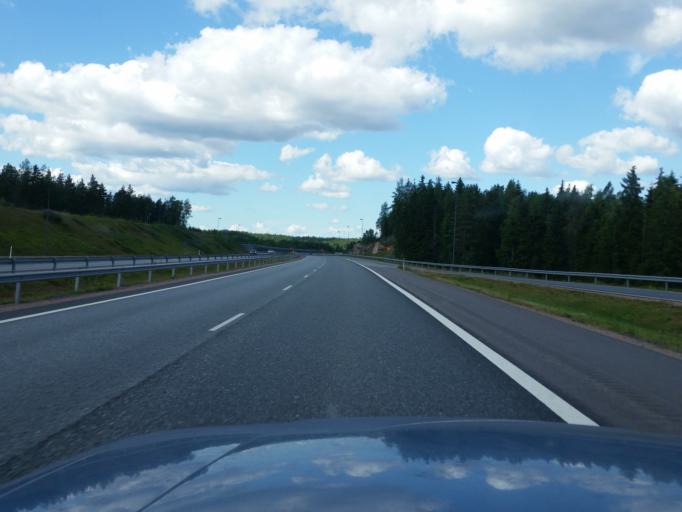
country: FI
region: Uusimaa
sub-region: Helsinki
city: Sammatti
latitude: 60.3694
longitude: 23.8576
